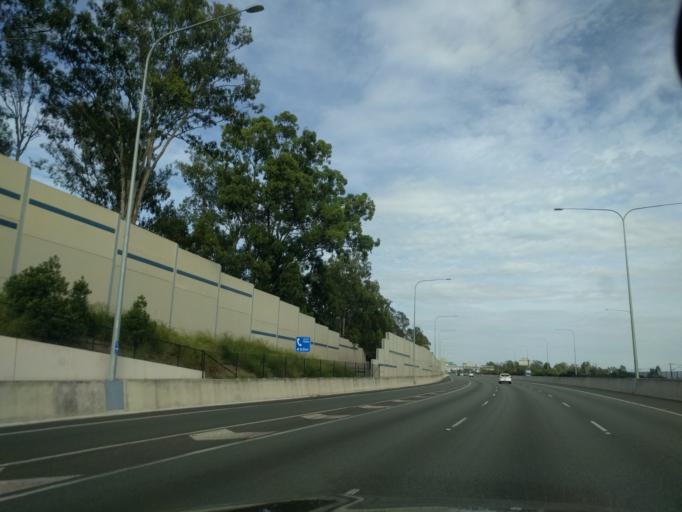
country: AU
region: Queensland
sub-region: Ipswich
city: Goodna
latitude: -27.6053
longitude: 152.8939
